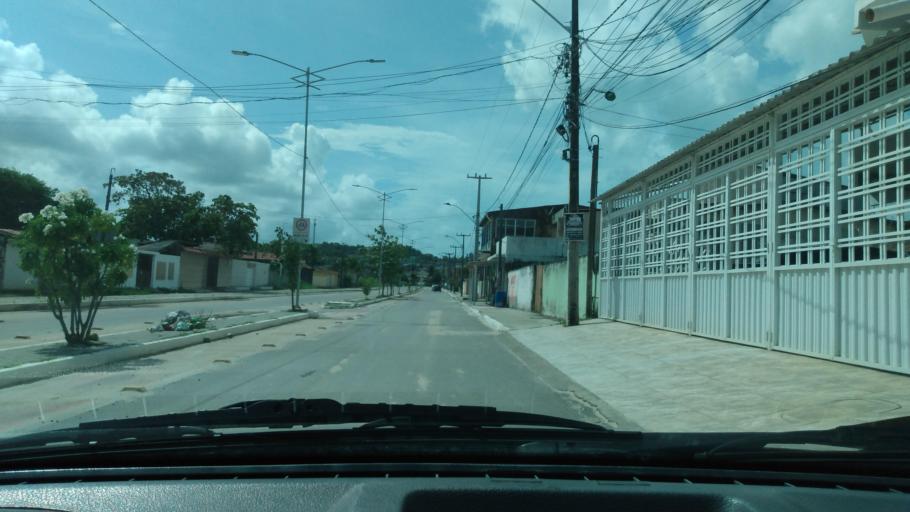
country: BR
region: Pernambuco
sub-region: Cabo De Santo Agostinho
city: Cabo
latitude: -8.3238
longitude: -34.9532
